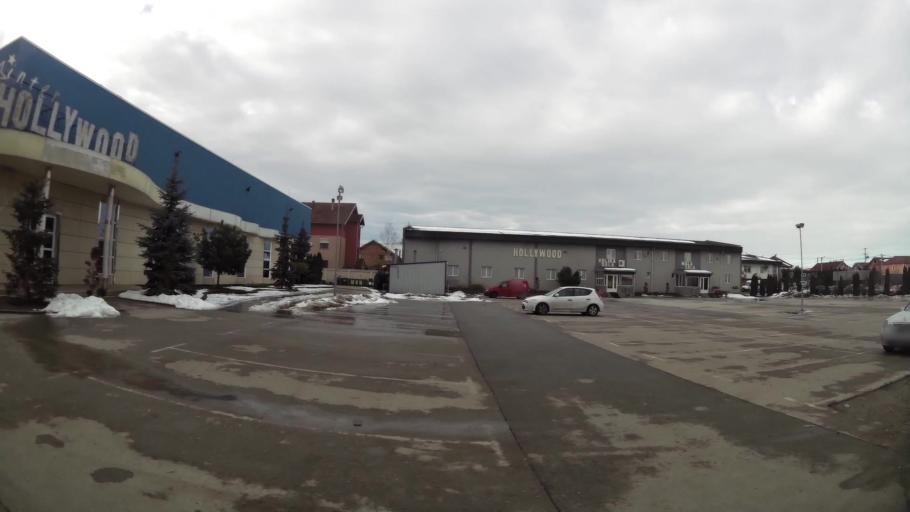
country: RS
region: Central Serbia
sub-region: Belgrade
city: Surcin
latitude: 44.8021
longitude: 20.3424
